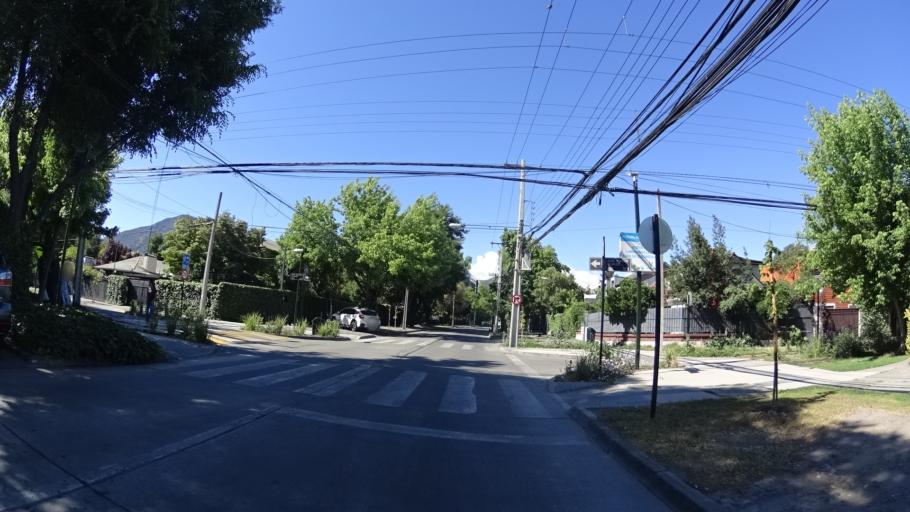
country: CL
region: Santiago Metropolitan
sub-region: Provincia de Santiago
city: Villa Presidente Frei, Nunoa, Santiago, Chile
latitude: -33.3946
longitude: -70.5943
